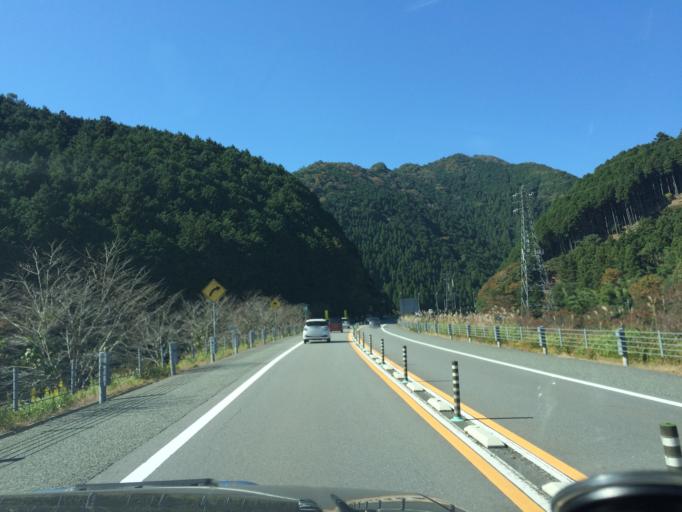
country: JP
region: Kyoto
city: Fukuchiyama
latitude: 35.2918
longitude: 134.9609
